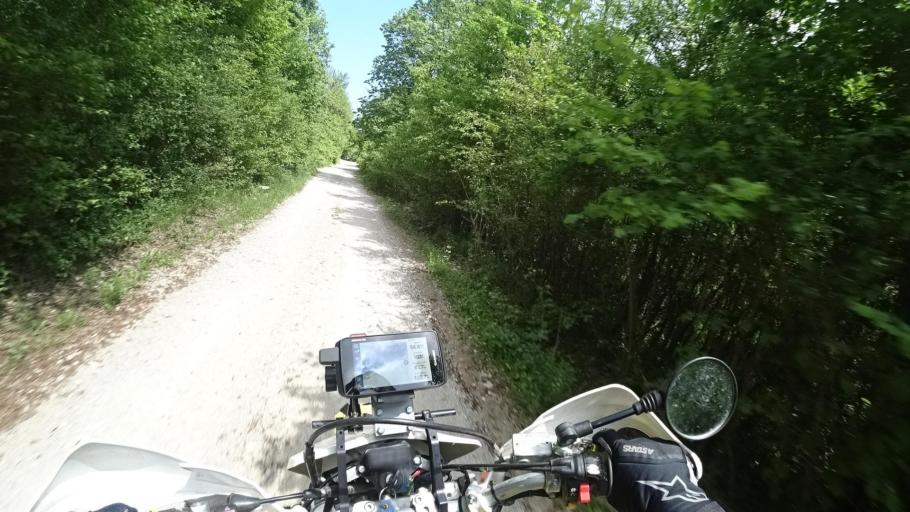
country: BA
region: Federation of Bosnia and Herzegovina
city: Ostrozac
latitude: 44.8335
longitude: 15.9831
